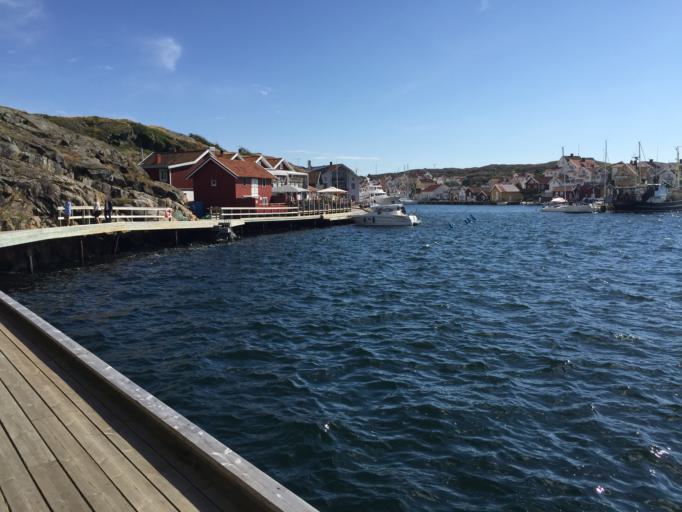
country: SE
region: Vaestra Goetaland
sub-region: Lysekils Kommun
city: Lysekil
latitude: 58.2179
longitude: 11.4163
